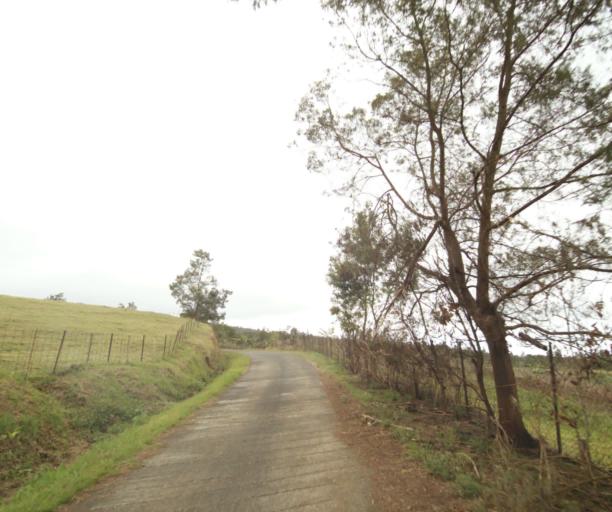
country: RE
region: Reunion
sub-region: Reunion
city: Saint-Paul
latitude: -21.0150
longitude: 55.3463
